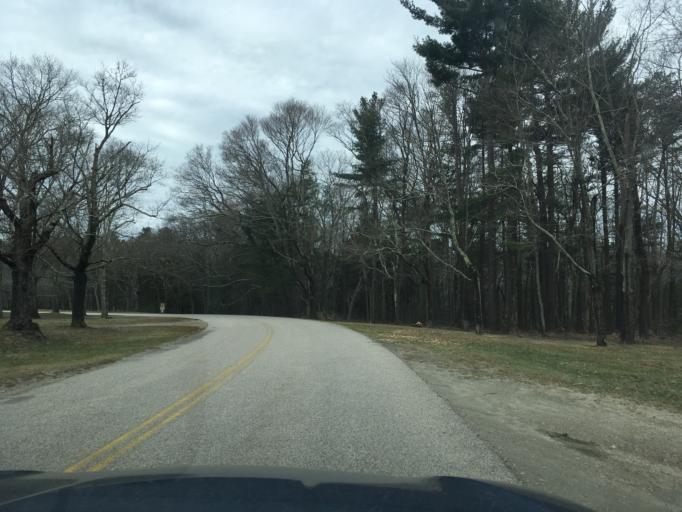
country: US
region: Rhode Island
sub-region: Kent County
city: East Greenwich
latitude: 41.6544
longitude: -71.4421
